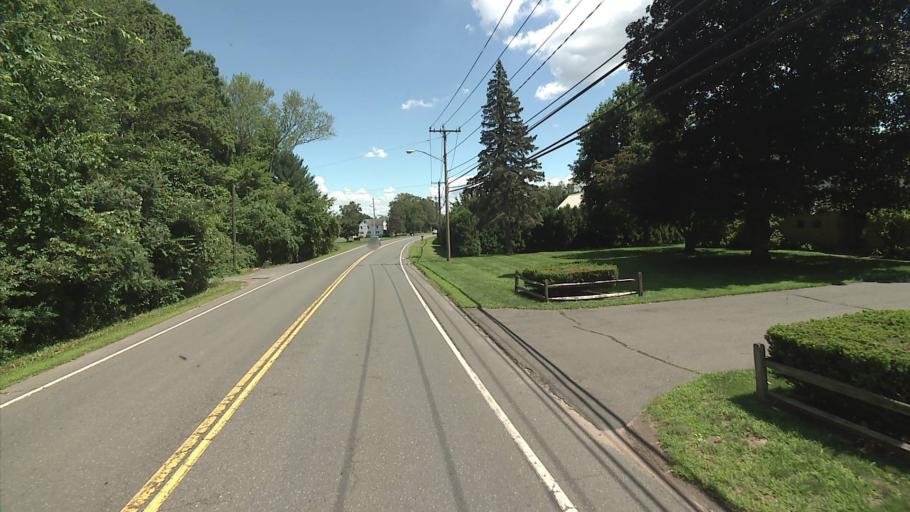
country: US
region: Connecticut
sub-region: Hartford County
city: Suffield Depot
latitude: 41.9901
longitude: -72.6972
